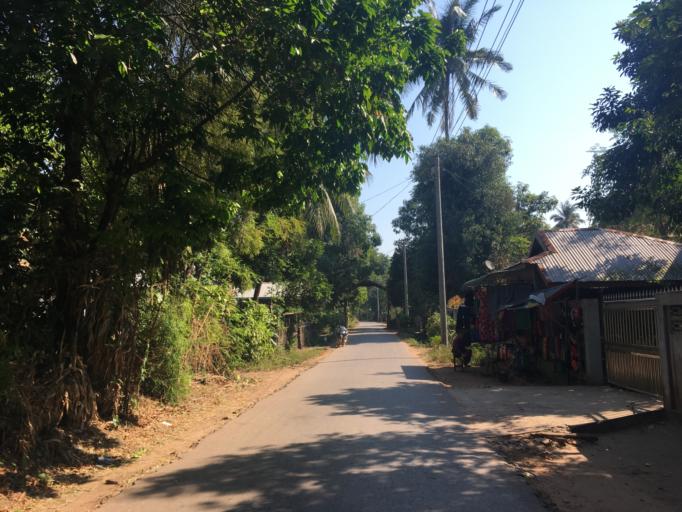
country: MM
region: Mon
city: Mawlamyine
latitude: 16.4321
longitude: 97.7001
